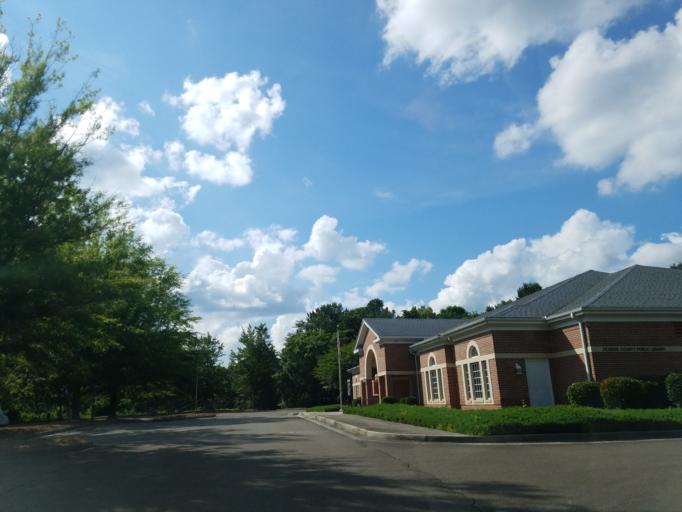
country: US
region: Georgia
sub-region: Pickens County
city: Jasper
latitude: 34.4739
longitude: -84.4212
